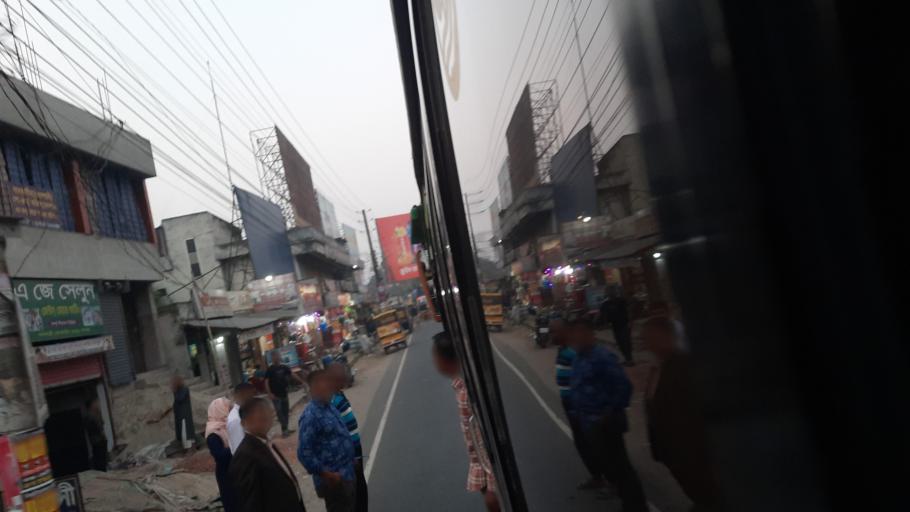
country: BD
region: Khulna
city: Jessore
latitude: 23.1805
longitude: 89.1912
